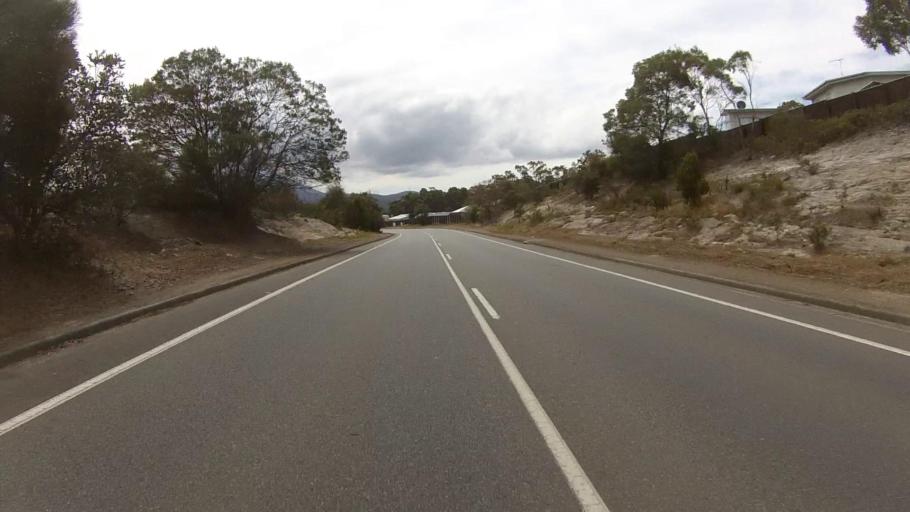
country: AU
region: Tasmania
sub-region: Kingborough
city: Kingston
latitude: -42.9911
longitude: 147.2942
